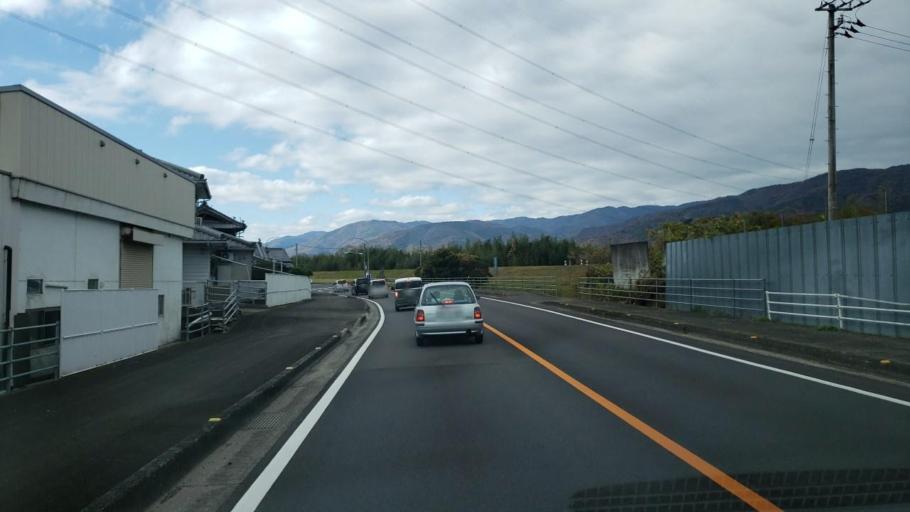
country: JP
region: Tokushima
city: Wakimachi
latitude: 34.0565
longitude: 134.1268
